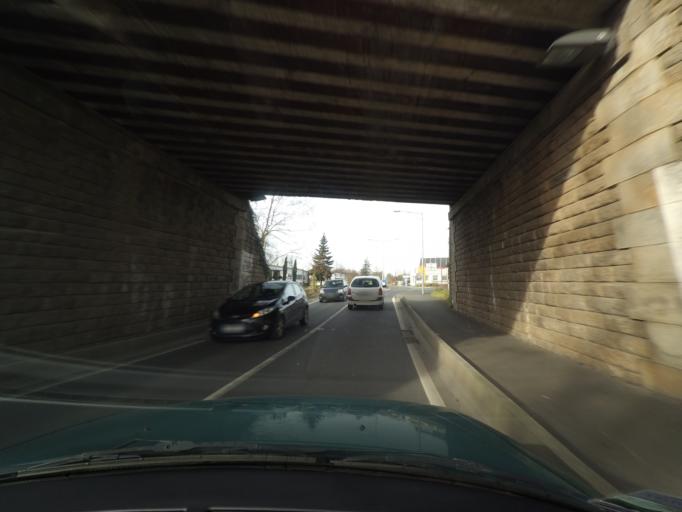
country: FR
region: Pays de la Loire
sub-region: Departement de la Vendee
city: Montaigu
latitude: 46.9826
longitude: -1.3180
